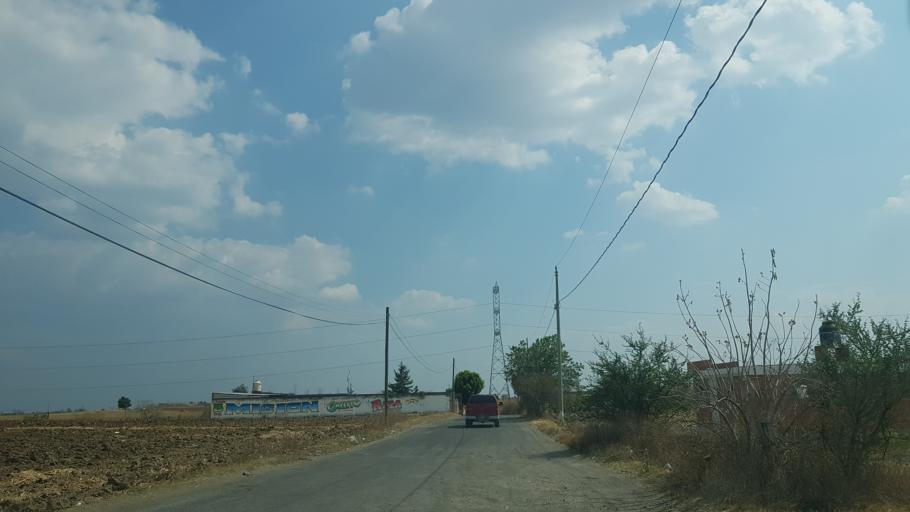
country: MX
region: Puebla
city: San Juan Amecac
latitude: 18.8254
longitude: -98.6556
